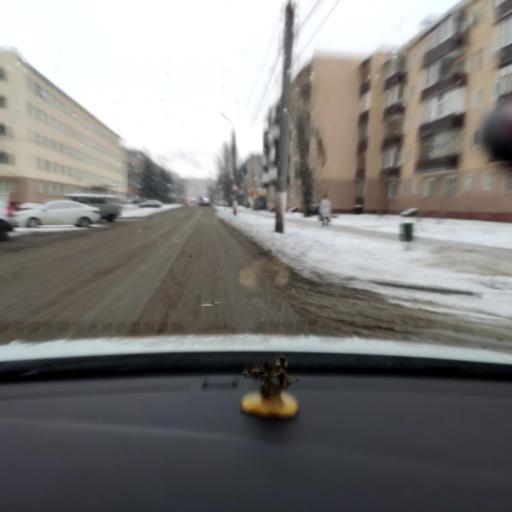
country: RU
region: Tatarstan
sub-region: Zelenodol'skiy Rayon
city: Zelenodolsk
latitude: 55.8505
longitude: 48.5250
